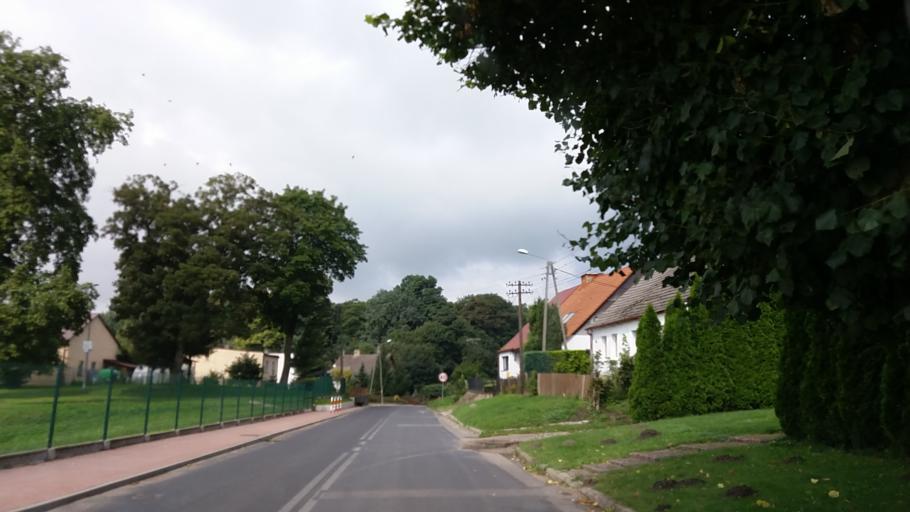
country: PL
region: West Pomeranian Voivodeship
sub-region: Powiat choszczenski
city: Krzecin
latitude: 53.0829
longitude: 15.4829
